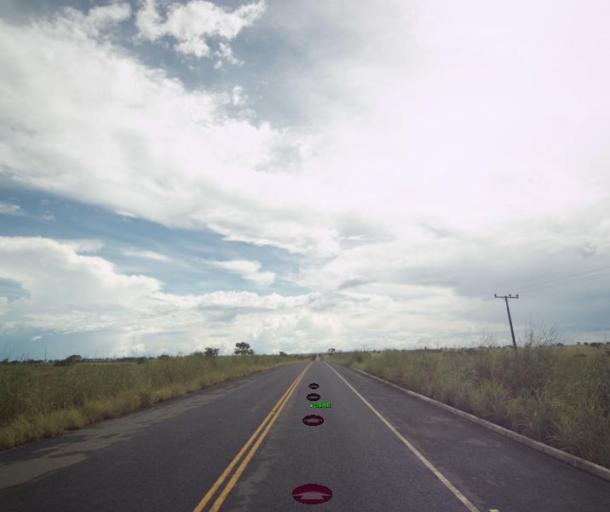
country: BR
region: Goias
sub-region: Sao Miguel Do Araguaia
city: Sao Miguel do Araguaia
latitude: -13.2916
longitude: -50.2165
